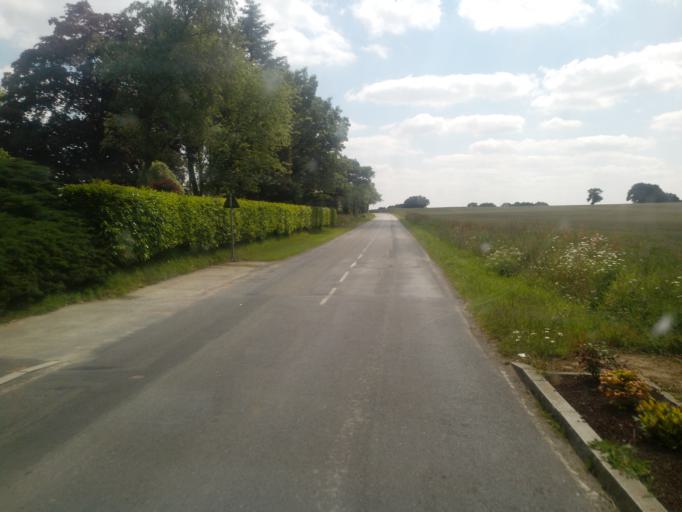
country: FR
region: Brittany
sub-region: Departement d'Ille-et-Vilaine
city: Montreuil-sur-Ille
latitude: 48.3258
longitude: -1.6441
